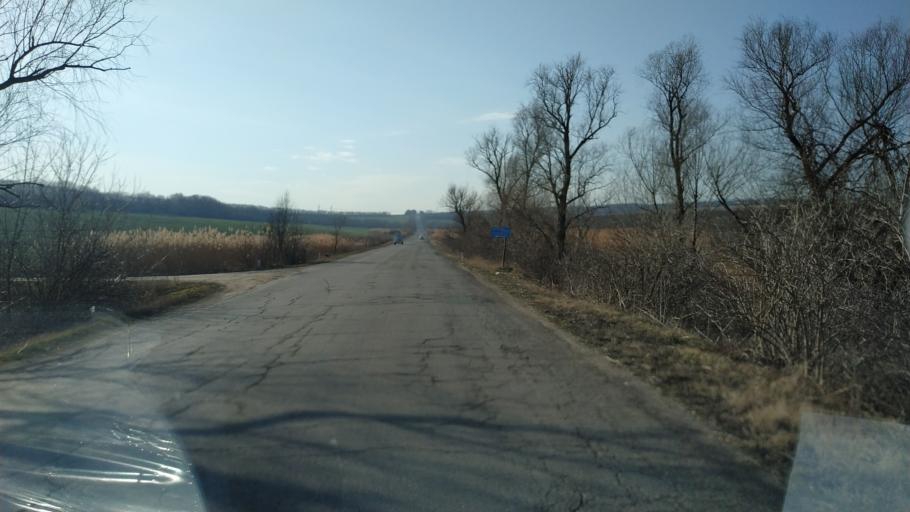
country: MD
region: Chisinau
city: Singera
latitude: 46.8870
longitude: 29.0392
